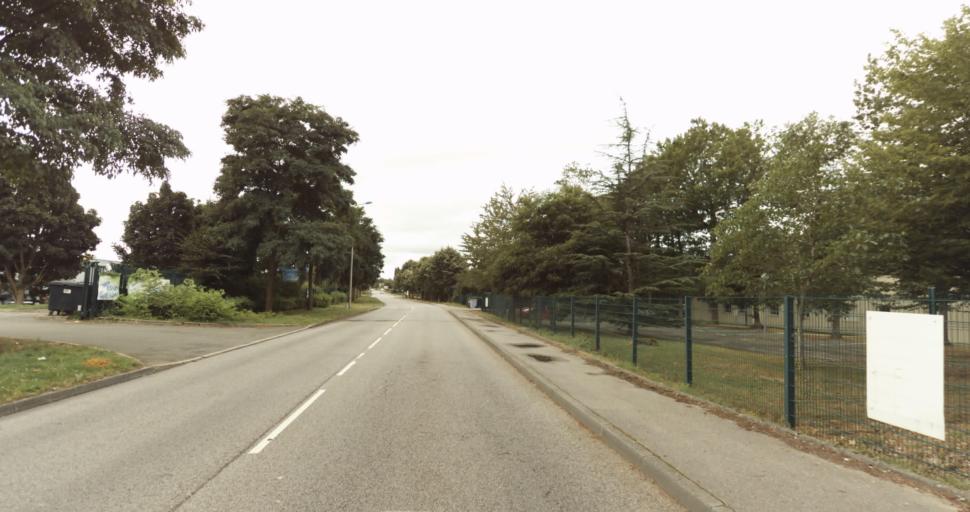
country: FR
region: Haute-Normandie
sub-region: Departement de l'Eure
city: Evreux
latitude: 49.0090
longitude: 1.1754
